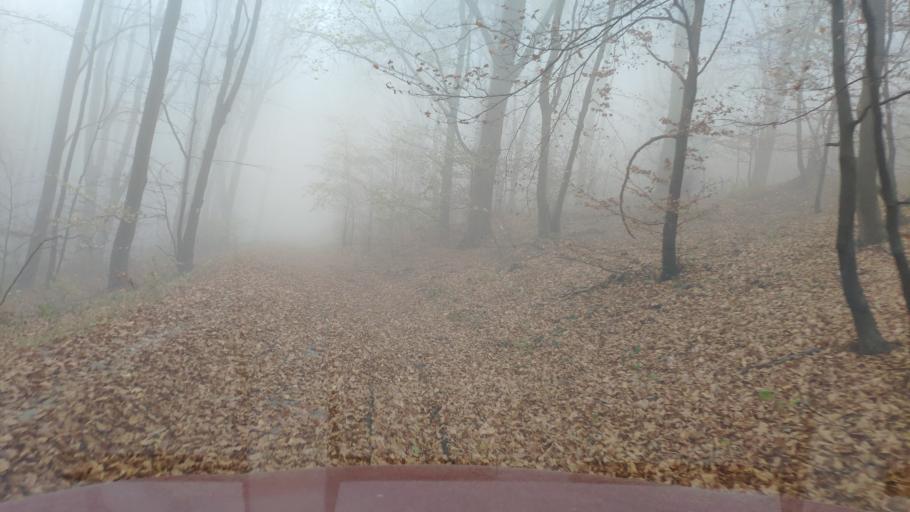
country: SK
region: Presovsky
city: Sabinov
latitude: 49.1529
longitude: 21.2267
